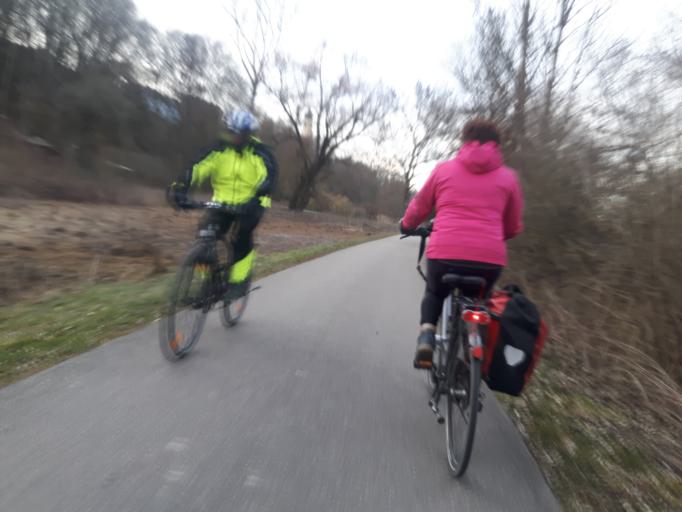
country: DE
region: Baden-Wuerttemberg
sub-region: Regierungsbezirk Stuttgart
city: Oedheim
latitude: 49.2477
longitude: 9.2928
